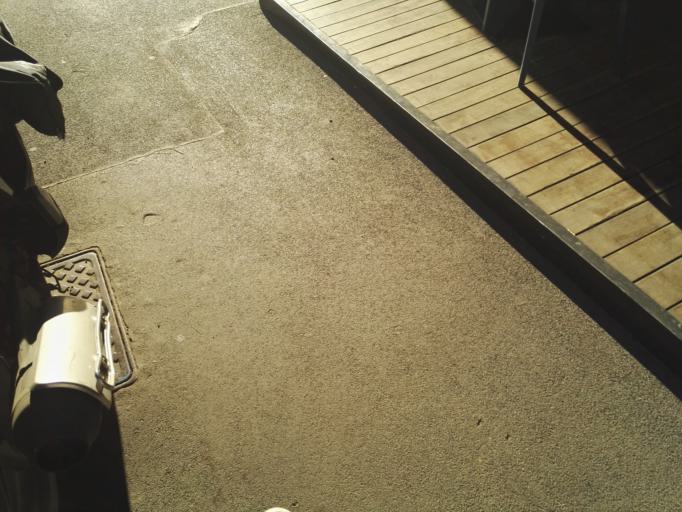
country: IT
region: Lombardy
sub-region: Citta metropolitana di Milano
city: Romano Banco
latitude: 45.4679
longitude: 9.1346
